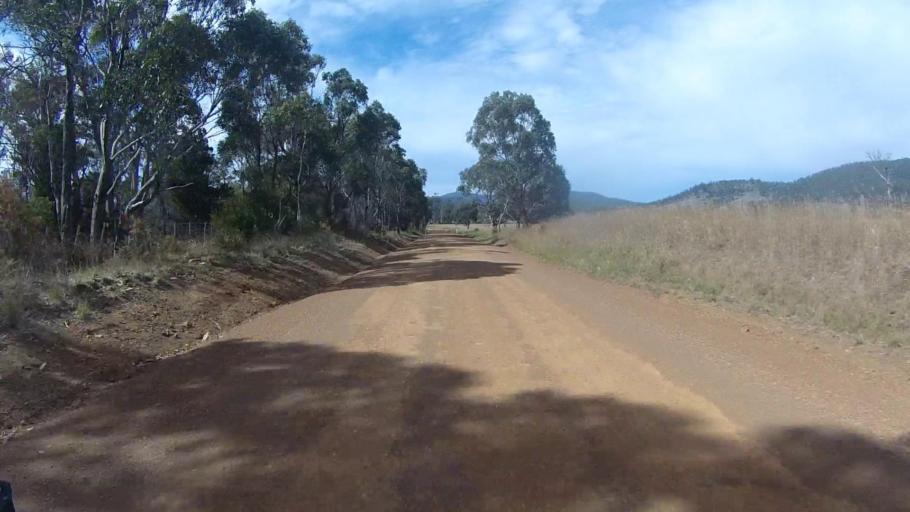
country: AU
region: Tasmania
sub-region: Sorell
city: Sorell
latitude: -42.6356
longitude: 147.9005
